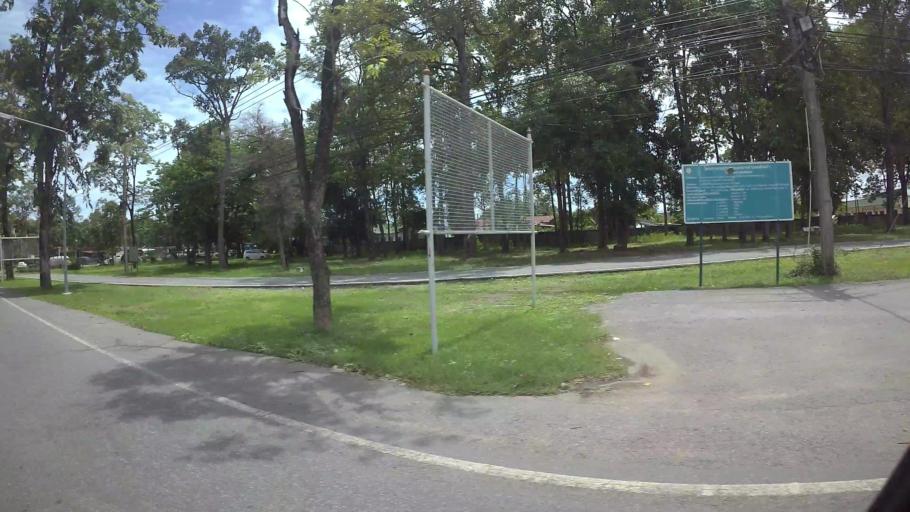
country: TH
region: Chon Buri
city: Sattahip
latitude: 12.7454
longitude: 100.8962
